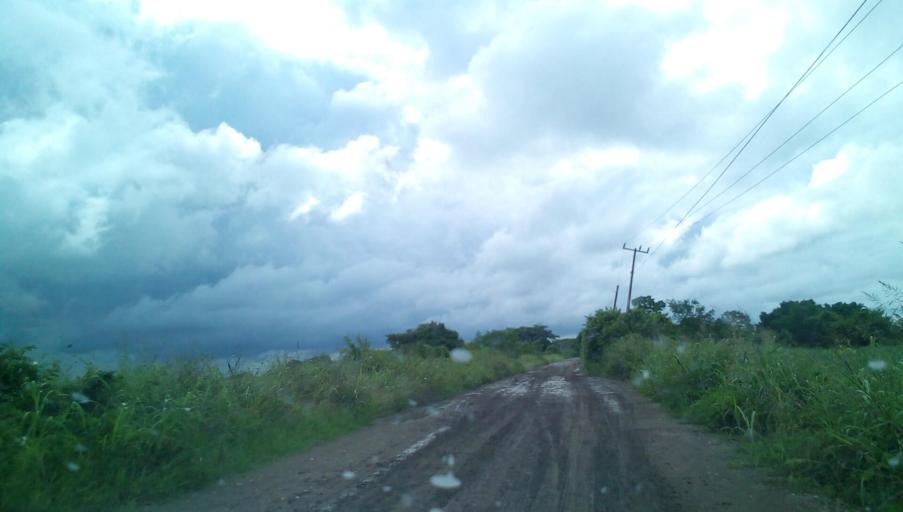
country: MX
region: Veracruz
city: Panuco
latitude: 21.8456
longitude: -98.1387
